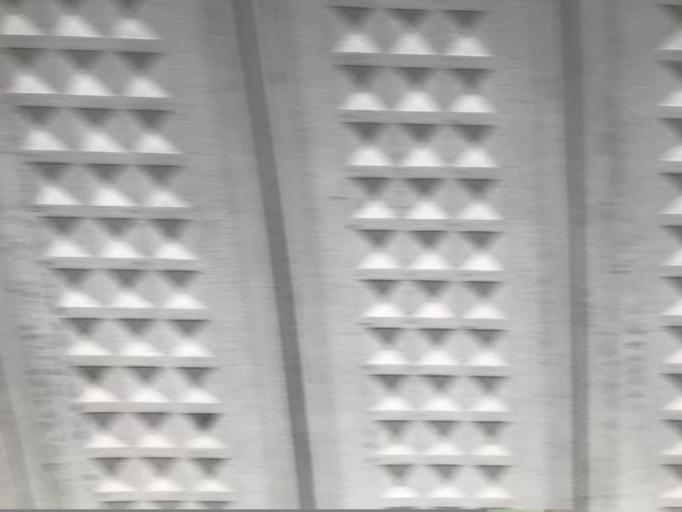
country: TR
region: Istanbul
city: Mahmutbey
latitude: 40.9840
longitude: 28.7758
